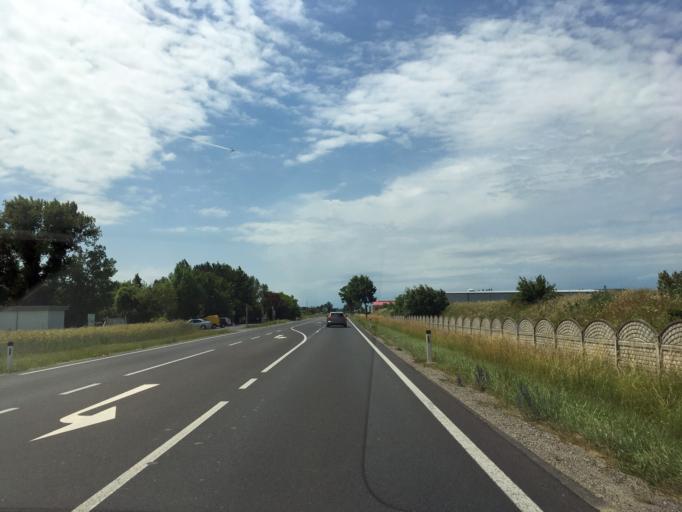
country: AT
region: Lower Austria
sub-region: Politischer Bezirk Baden
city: Teesdorf
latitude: 47.9698
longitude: 16.2776
